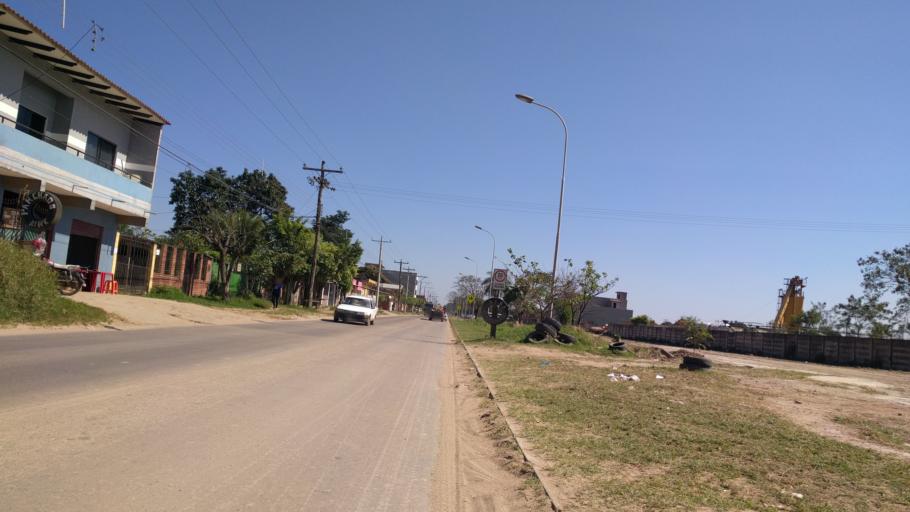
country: BO
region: Santa Cruz
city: Santa Cruz de la Sierra
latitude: -17.8512
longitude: -63.2006
